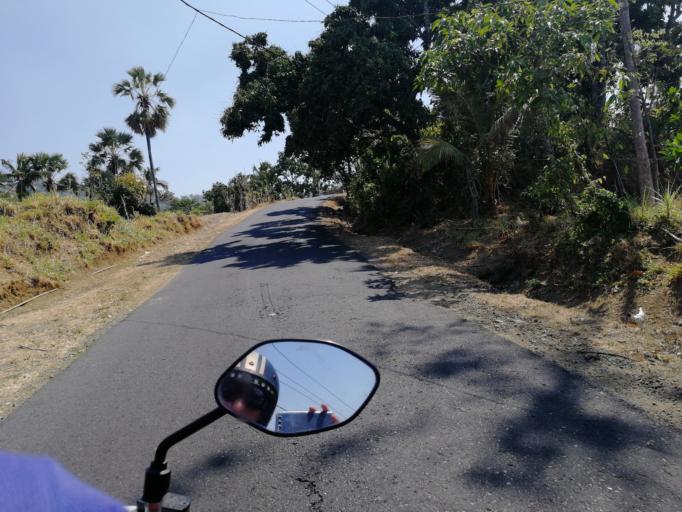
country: ID
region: Bali
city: Banjar Trunyan
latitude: -8.1359
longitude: 115.3234
